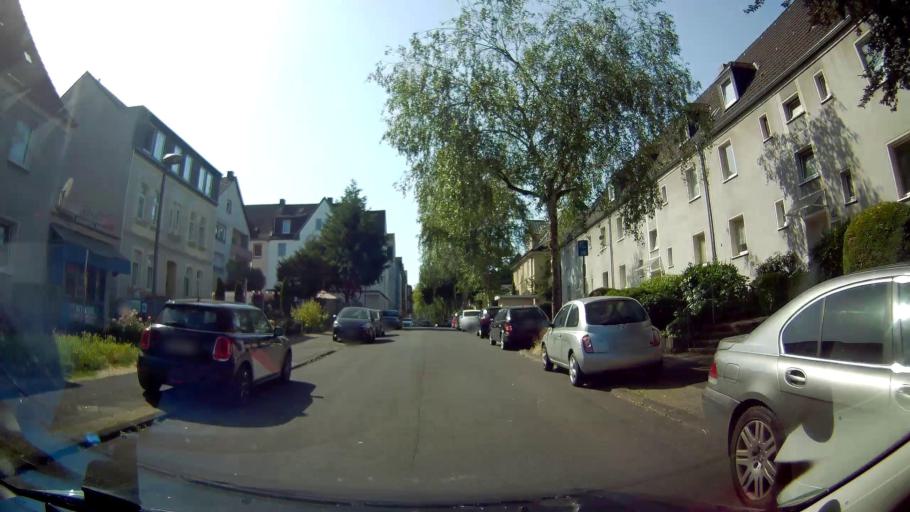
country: DE
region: North Rhine-Westphalia
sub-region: Regierungsbezirk Arnsberg
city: Bochum
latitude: 51.5105
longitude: 7.2090
